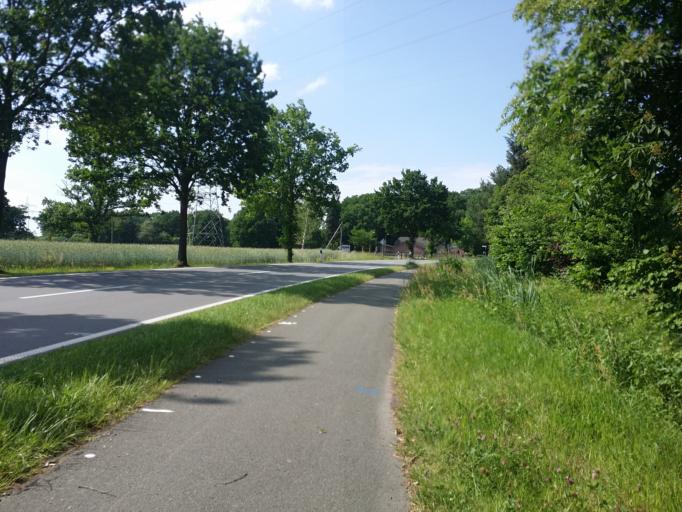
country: DE
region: Lower Saxony
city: Rastede
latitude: 53.2286
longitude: 8.1741
